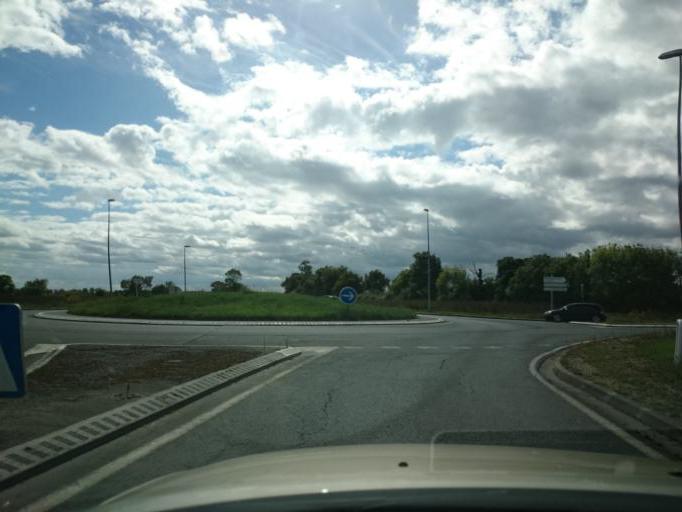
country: FR
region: Aquitaine
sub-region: Departement de la Gironde
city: Saint-Louis-de-Montferrand
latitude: 44.9441
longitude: -0.5599
